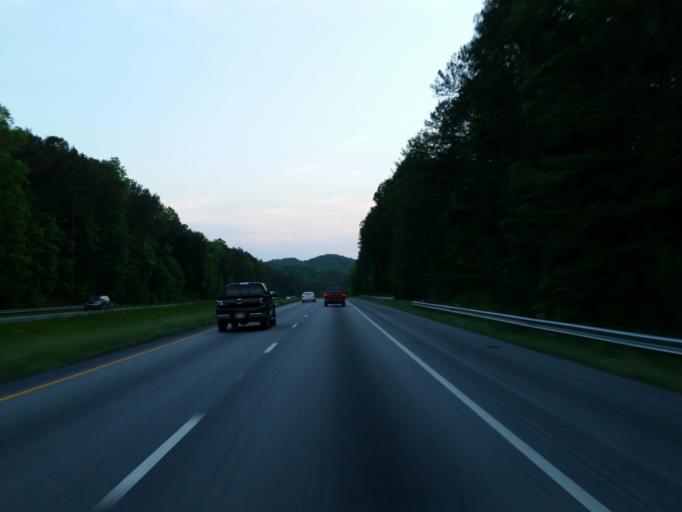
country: US
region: Alabama
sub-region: Calhoun County
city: Choccolocco
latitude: 33.6169
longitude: -85.6660
